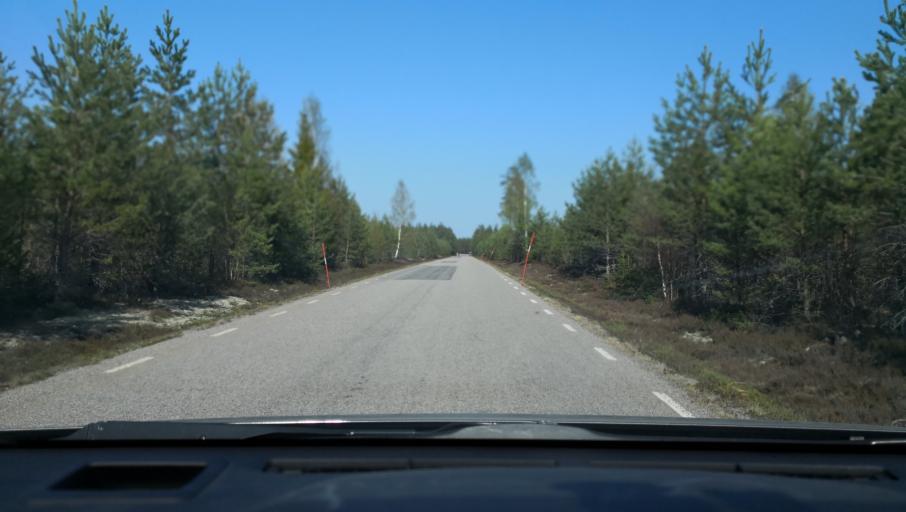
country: SE
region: Uppsala
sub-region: Heby Kommun
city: Heby
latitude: 60.0478
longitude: 16.8585
